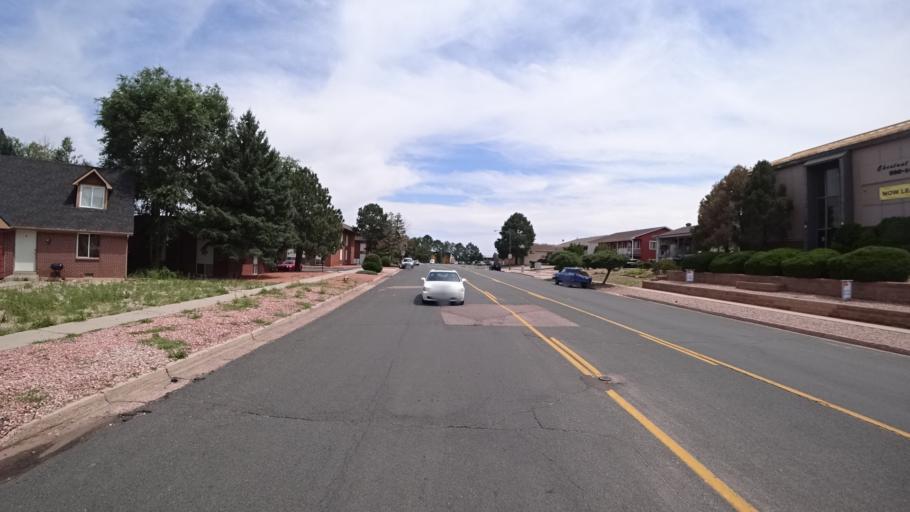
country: US
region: Colorado
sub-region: El Paso County
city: Colorado Springs
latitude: 38.8932
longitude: -104.8354
